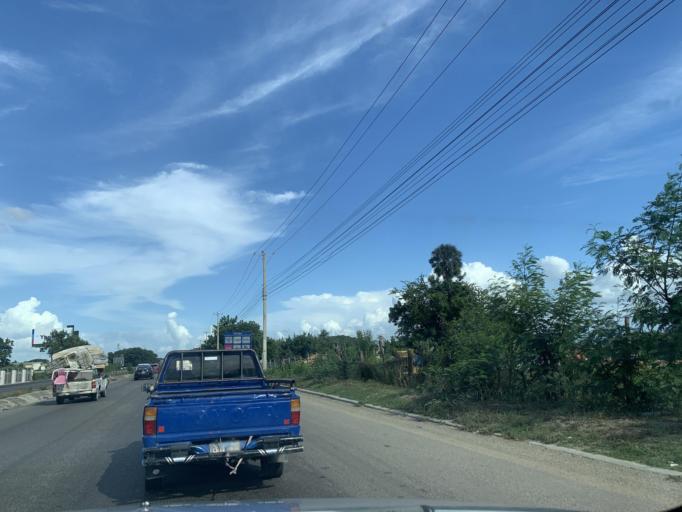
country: DO
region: Santiago
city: Villa Gonzalez
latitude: 19.5414
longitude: -70.7978
